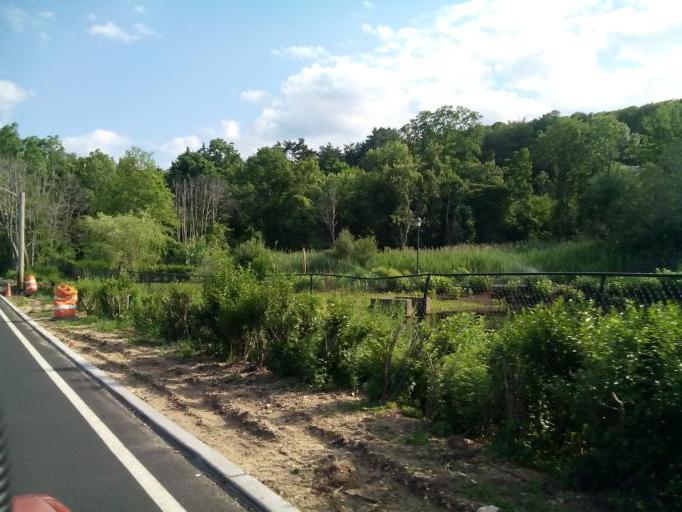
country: US
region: New York
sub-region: Nassau County
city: Oyster Bay
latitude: 40.8787
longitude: -73.5437
